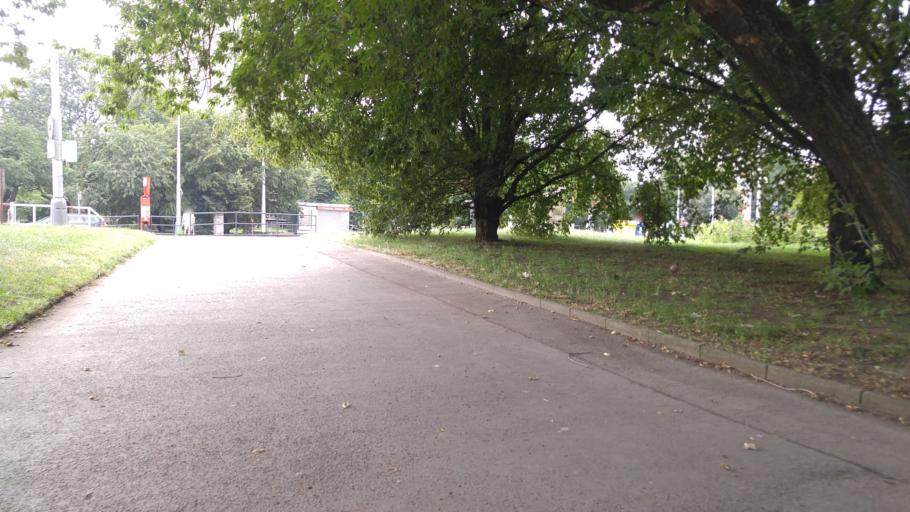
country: CZ
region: Central Bohemia
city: Horomerice
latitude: 50.0901
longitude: 14.3511
